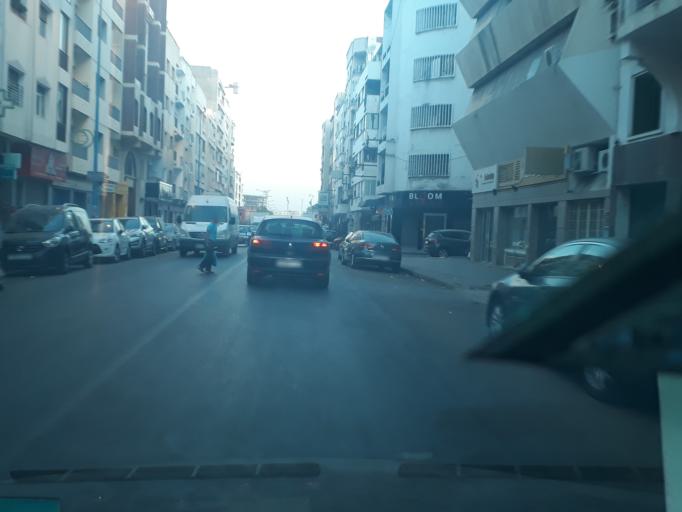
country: MA
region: Grand Casablanca
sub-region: Casablanca
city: Casablanca
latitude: 33.5774
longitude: -7.6448
